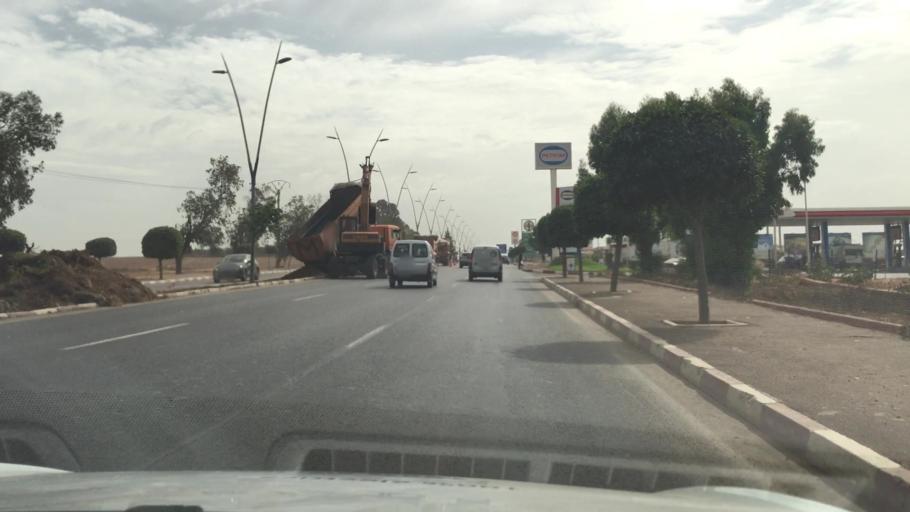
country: MA
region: Grand Casablanca
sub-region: Nouaceur
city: Bouskoura
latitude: 33.5105
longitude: -7.6305
